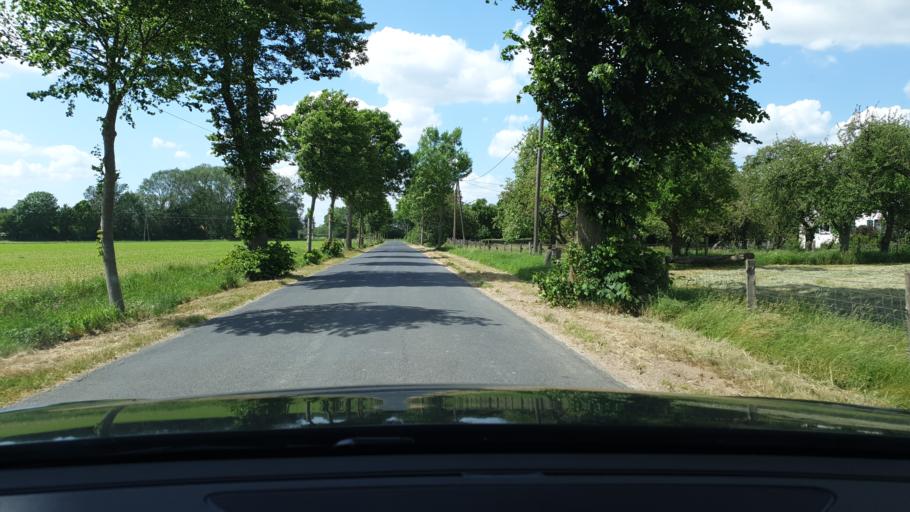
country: DE
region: North Rhine-Westphalia
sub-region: Regierungsbezirk Dusseldorf
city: Kleve
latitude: 51.8064
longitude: 6.0808
